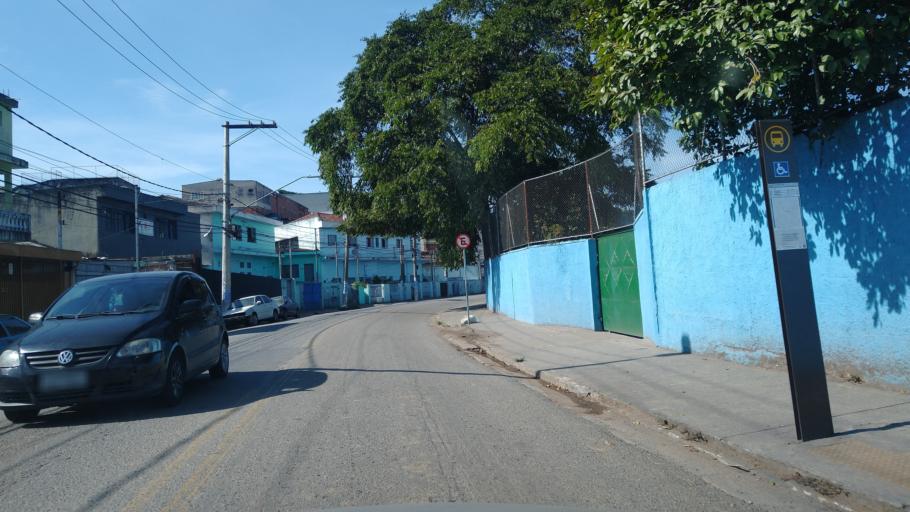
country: BR
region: Sao Paulo
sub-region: Sao Paulo
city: Sao Paulo
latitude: -23.4638
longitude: -46.6689
